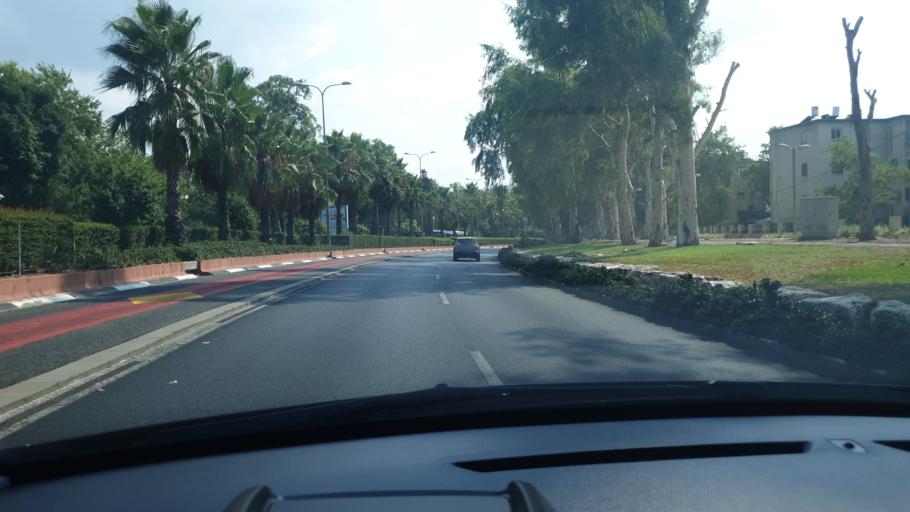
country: IL
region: Haifa
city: Qiryat Bialik
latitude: 32.8202
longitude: 35.0791
